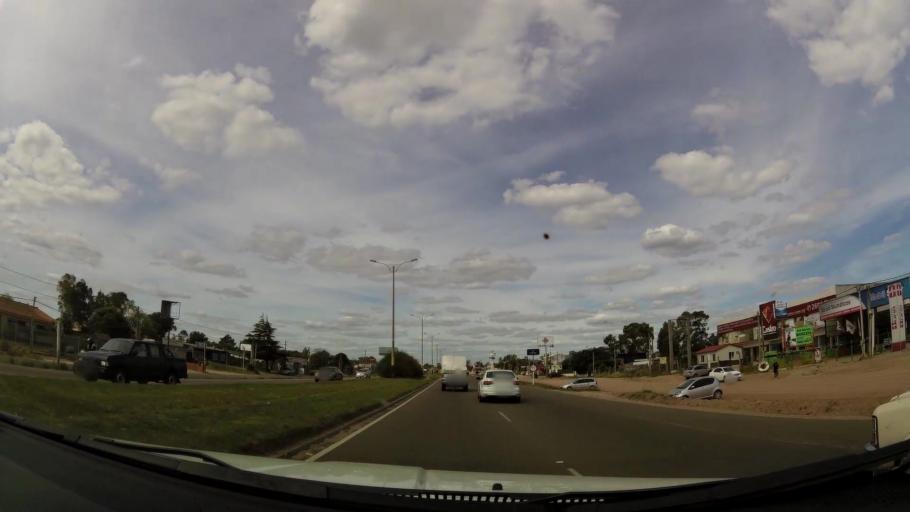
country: UY
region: Canelones
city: Colonia Nicolich
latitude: -34.8304
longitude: -55.9742
